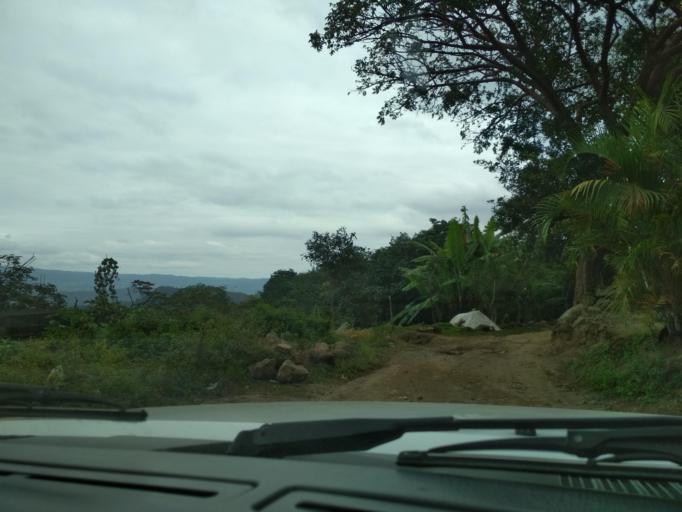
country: MX
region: Veracruz
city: El Castillo
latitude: 19.5786
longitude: -96.8608
